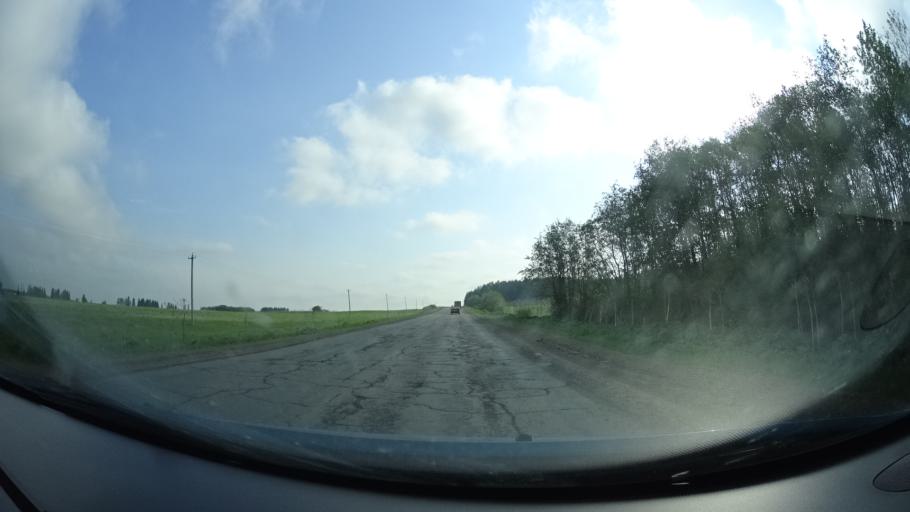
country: RU
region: Perm
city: Kultayevo
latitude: 57.8565
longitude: 55.8597
